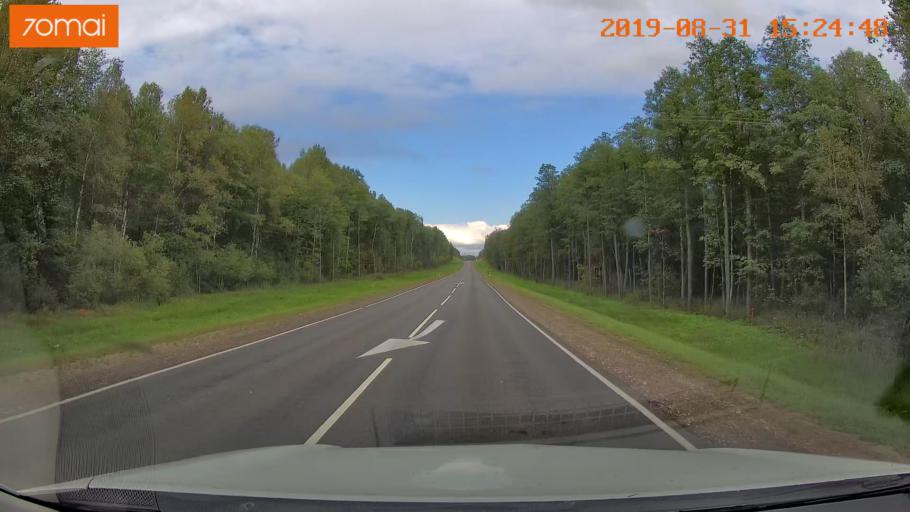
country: RU
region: Kaluga
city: Baryatino
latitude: 54.5326
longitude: 34.5101
